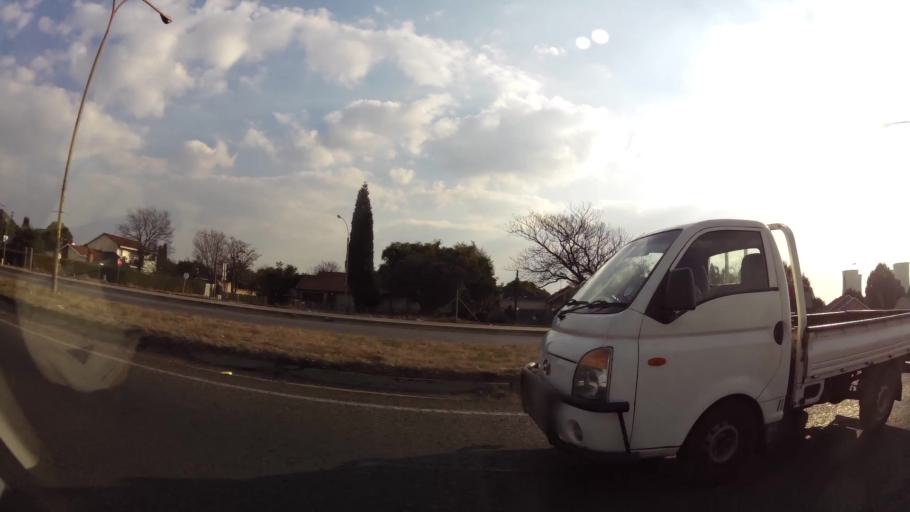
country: ZA
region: Gauteng
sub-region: City of Johannesburg Metropolitan Municipality
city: Modderfontein
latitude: -26.1244
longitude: 28.2015
